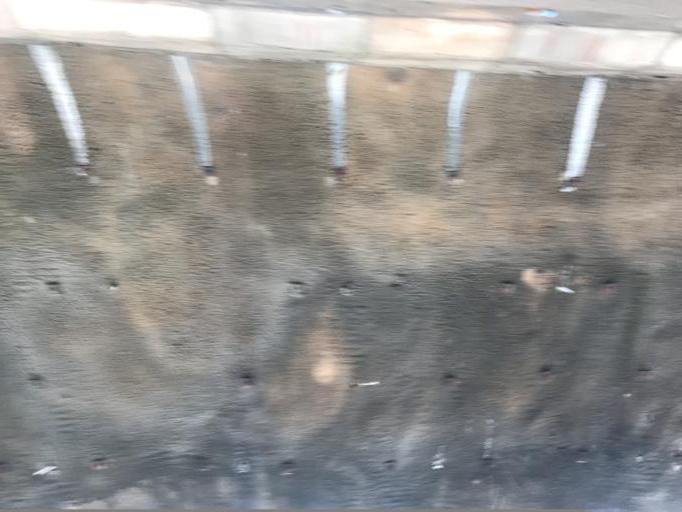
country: TR
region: Bartin
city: Amasra
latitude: 41.7191
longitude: 32.3948
